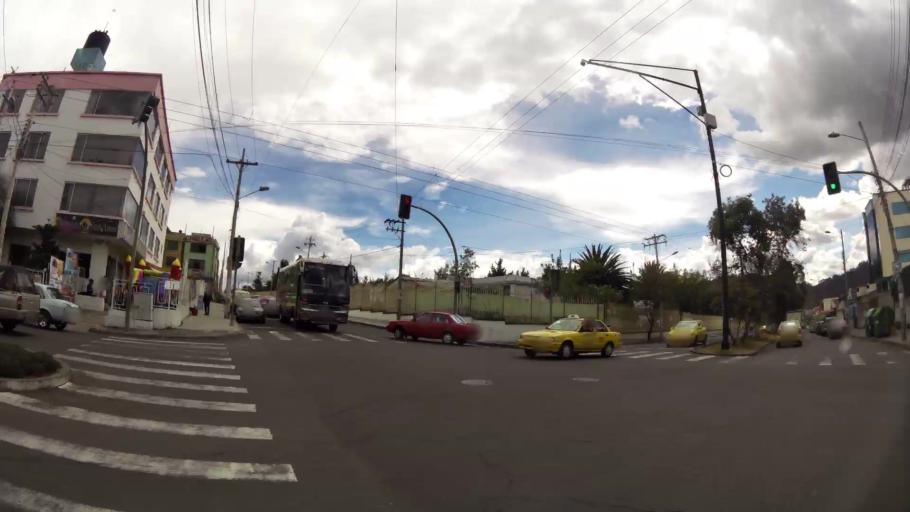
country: EC
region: Tungurahua
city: Ambato
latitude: -1.2515
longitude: -78.6250
